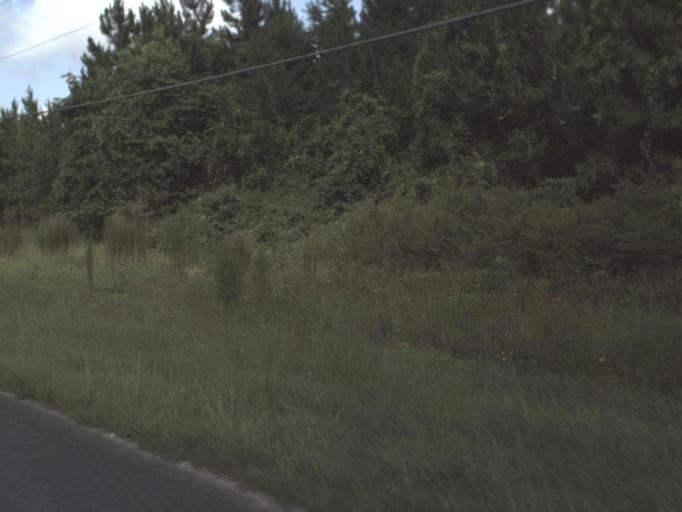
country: US
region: Florida
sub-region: Columbia County
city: Lake City
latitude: 30.1467
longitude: -82.6995
